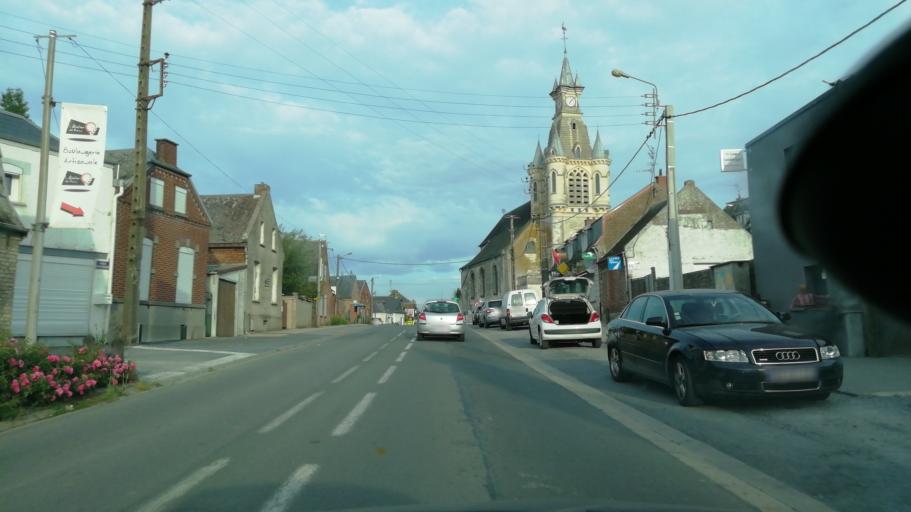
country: FR
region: Nord-Pas-de-Calais
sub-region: Departement du Nord
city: Viesly
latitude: 50.1229
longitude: 3.4604
